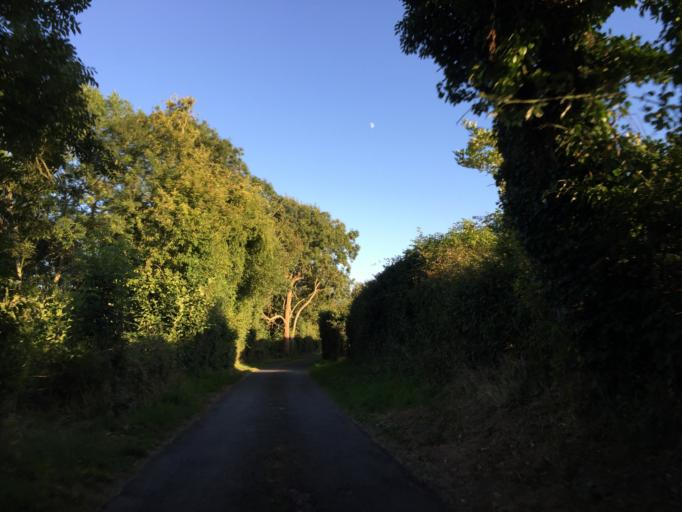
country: FR
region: Lower Normandy
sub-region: Departement du Calvados
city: Equemauville
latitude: 49.4009
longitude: 0.1964
